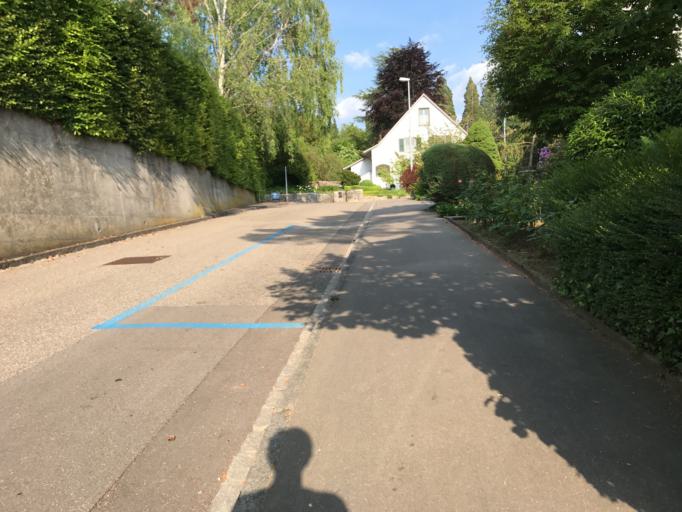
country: CH
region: Basel-City
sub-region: Basel-Stadt
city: Riehen
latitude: 47.5738
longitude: 7.6493
